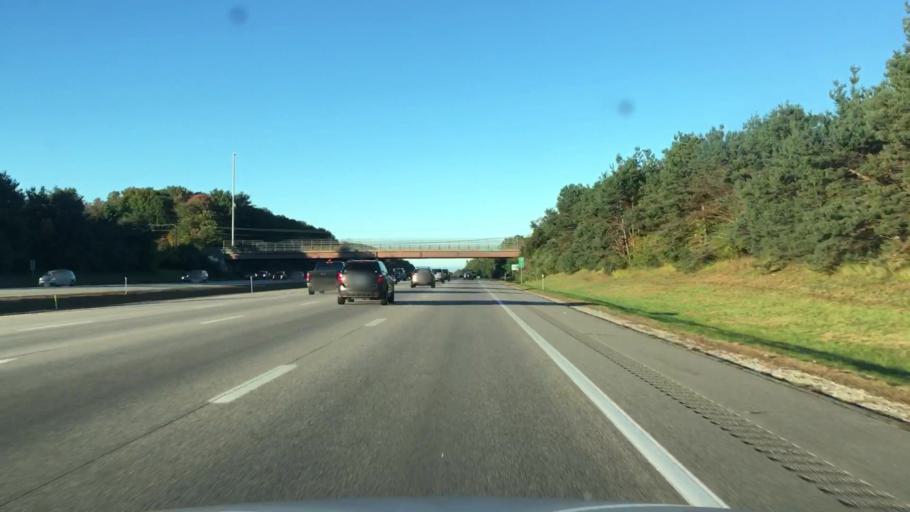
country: US
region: New Hampshire
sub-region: Rockingham County
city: Greenland
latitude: 43.0187
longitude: -70.8312
